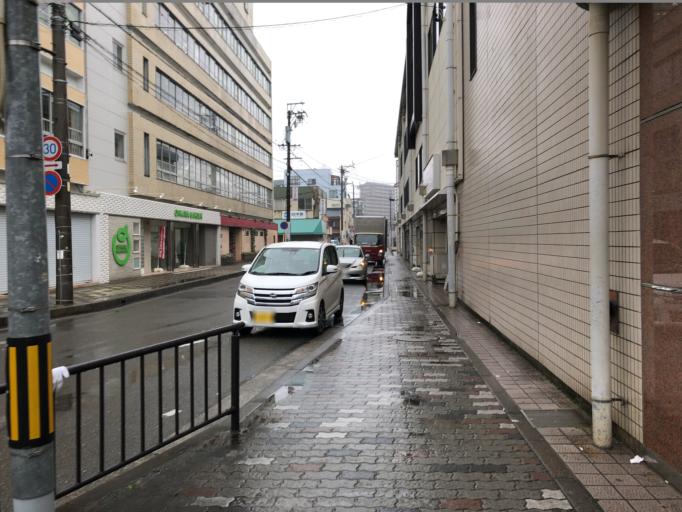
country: JP
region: Mie
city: Tsu-shi
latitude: 34.7337
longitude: 136.5101
